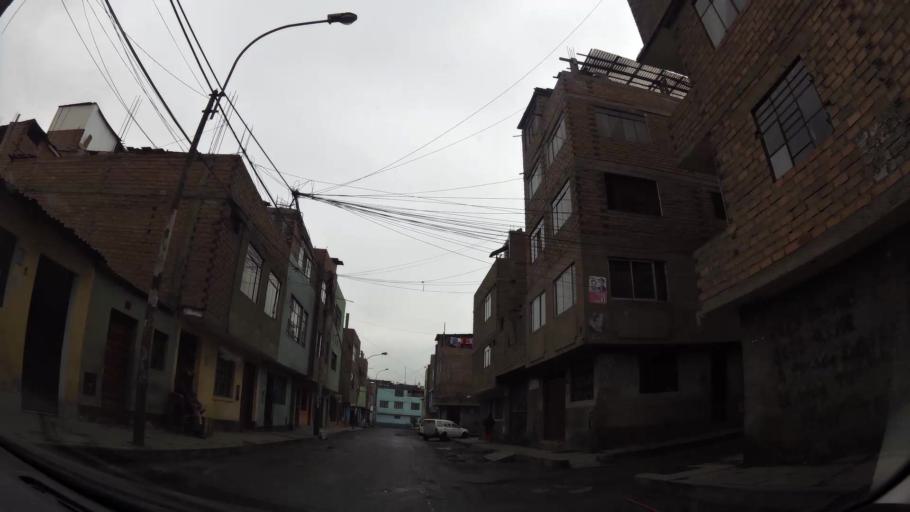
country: PE
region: Lima
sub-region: Lima
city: San Luis
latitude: -12.0517
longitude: -77.0009
